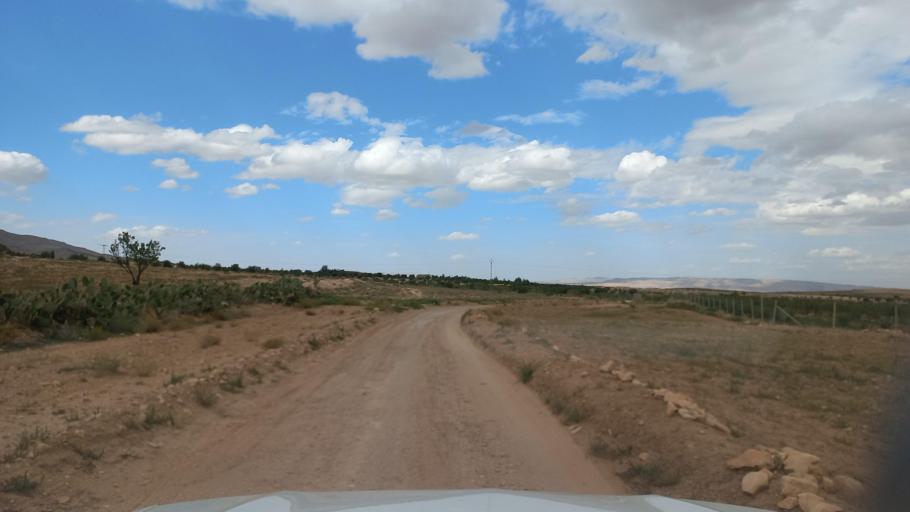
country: TN
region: Al Qasrayn
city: Sbiba
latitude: 35.4349
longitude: 9.0977
